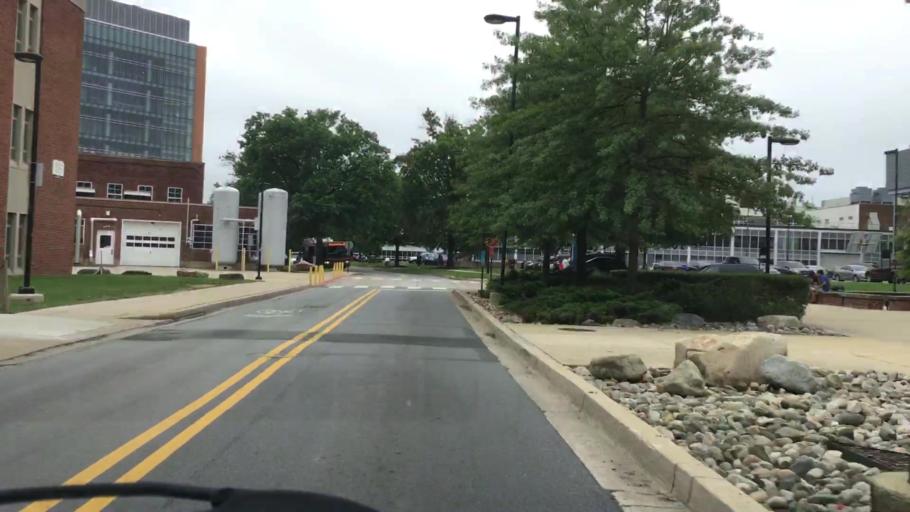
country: US
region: Maryland
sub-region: Prince George's County
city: College Park
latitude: 38.9906
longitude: -76.9373
